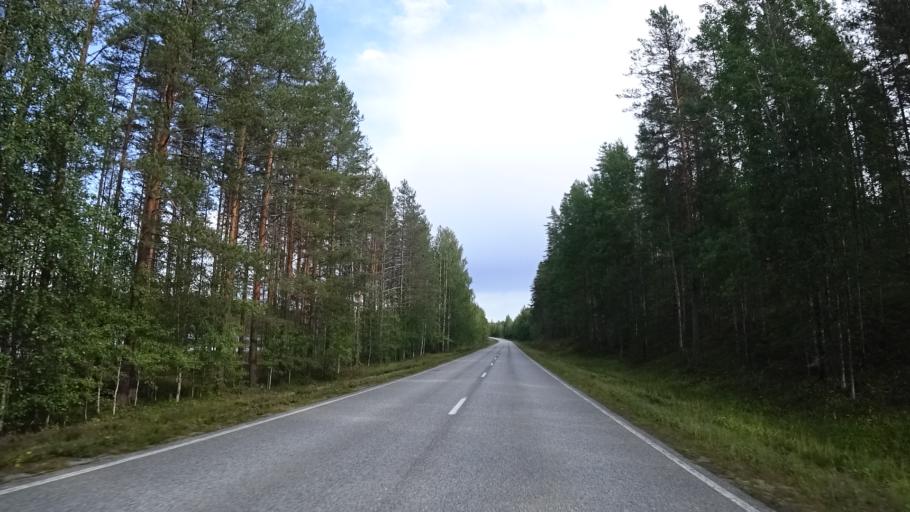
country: FI
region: North Karelia
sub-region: Joensuu
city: Ilomantsi
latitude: 62.6254
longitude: 31.1095
